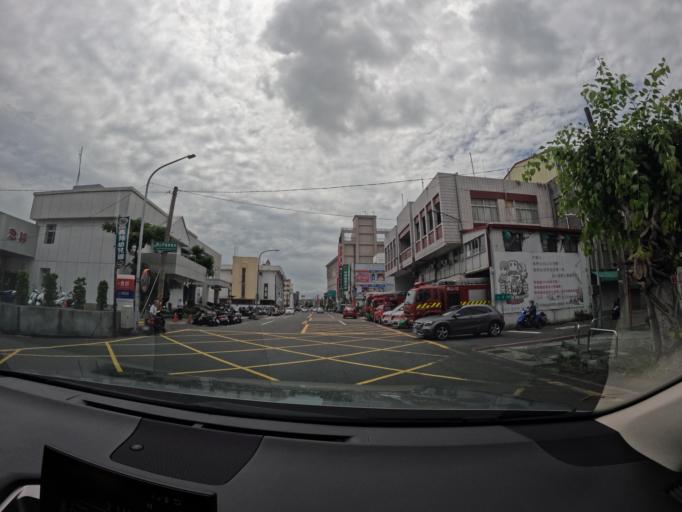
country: TW
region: Kaohsiung
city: Kaohsiung
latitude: 22.7964
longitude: 120.2942
